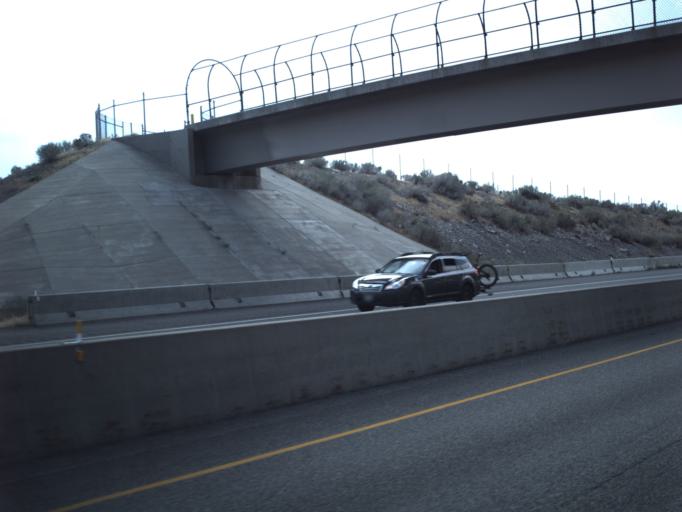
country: US
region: Utah
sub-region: Salt Lake County
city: East Millcreek
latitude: 40.7124
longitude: -111.8021
